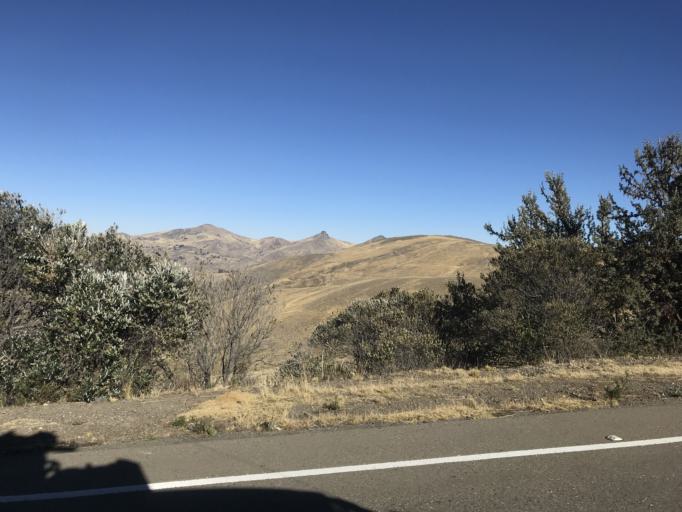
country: PE
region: Puno
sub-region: Yunguyo
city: Yunguyo
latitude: -16.1715
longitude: -68.9831
